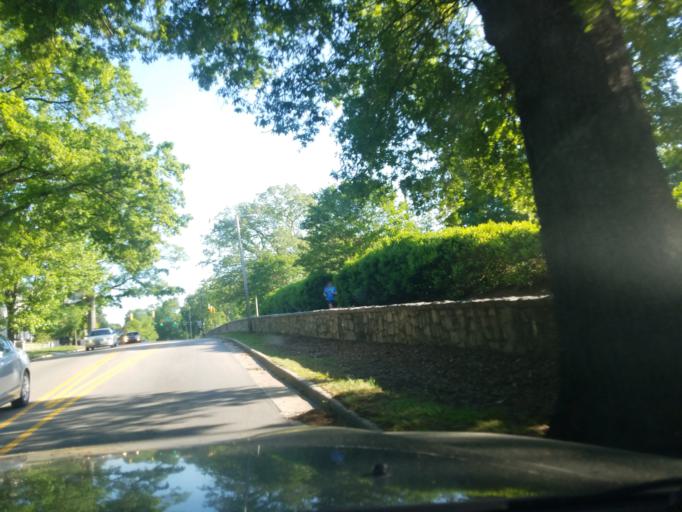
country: US
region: North Carolina
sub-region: Durham County
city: Durham
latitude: 36.0066
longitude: -78.9124
